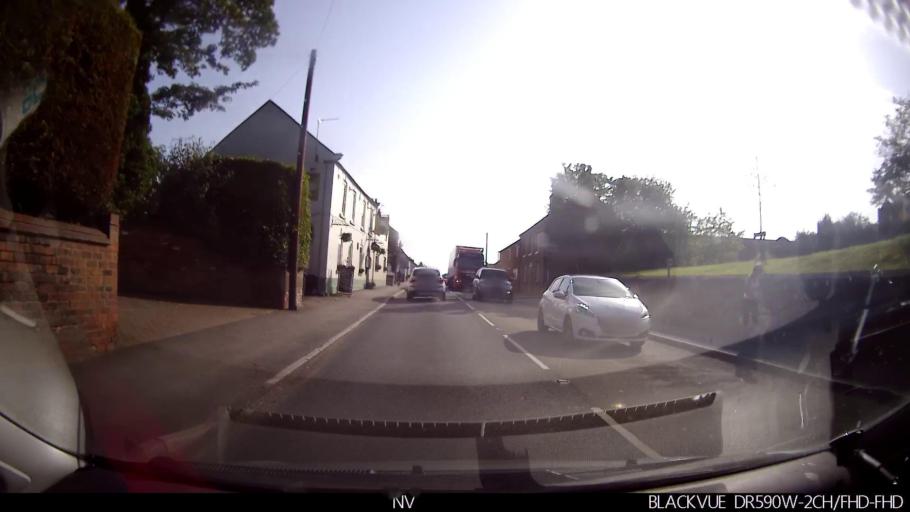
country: GB
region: England
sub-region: North Yorkshire
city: Thorpe Bassett
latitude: 54.1575
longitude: -0.6959
